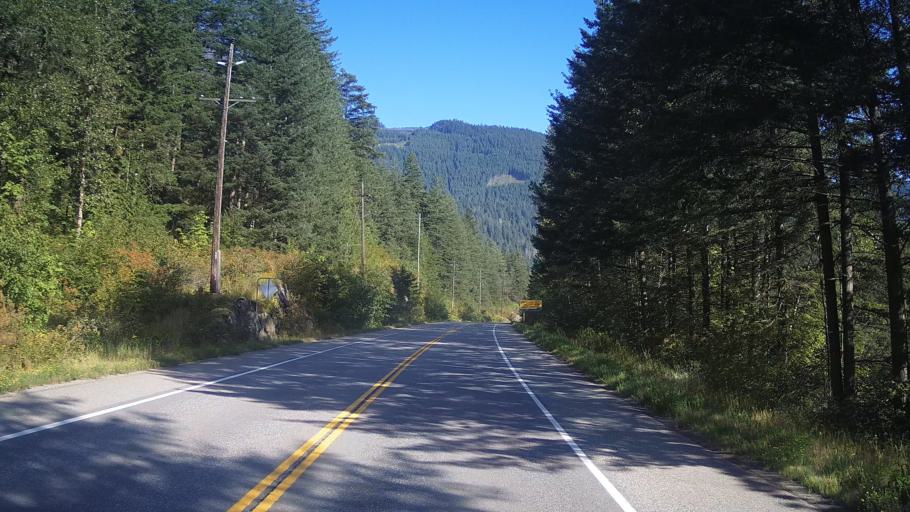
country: CA
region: British Columbia
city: Hope
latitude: 49.5413
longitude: -121.4365
